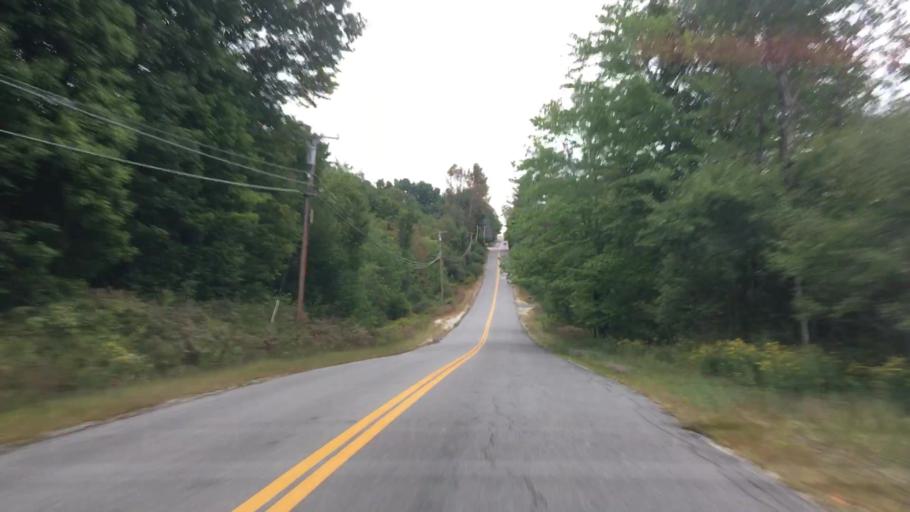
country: US
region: Maine
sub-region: Cumberland County
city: Freeport
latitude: 43.8944
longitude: -70.1889
